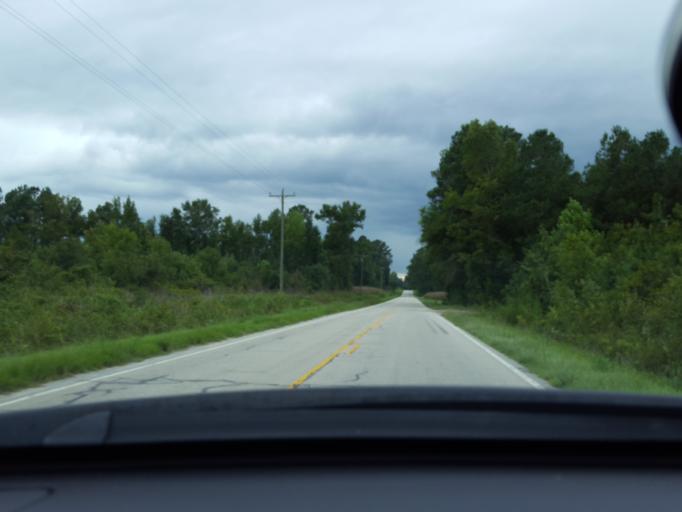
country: US
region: North Carolina
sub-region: Duplin County
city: Rose Hill
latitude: 34.8082
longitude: -78.1997
